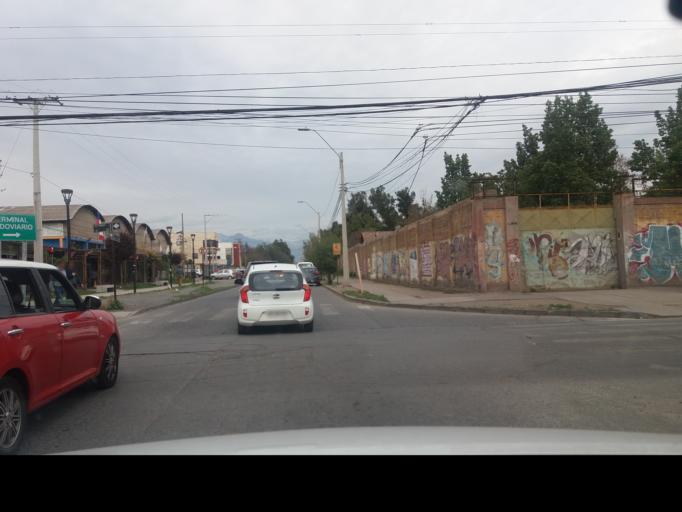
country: CL
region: Valparaiso
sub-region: Provincia de San Felipe
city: San Felipe
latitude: -32.7548
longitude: -70.7211
